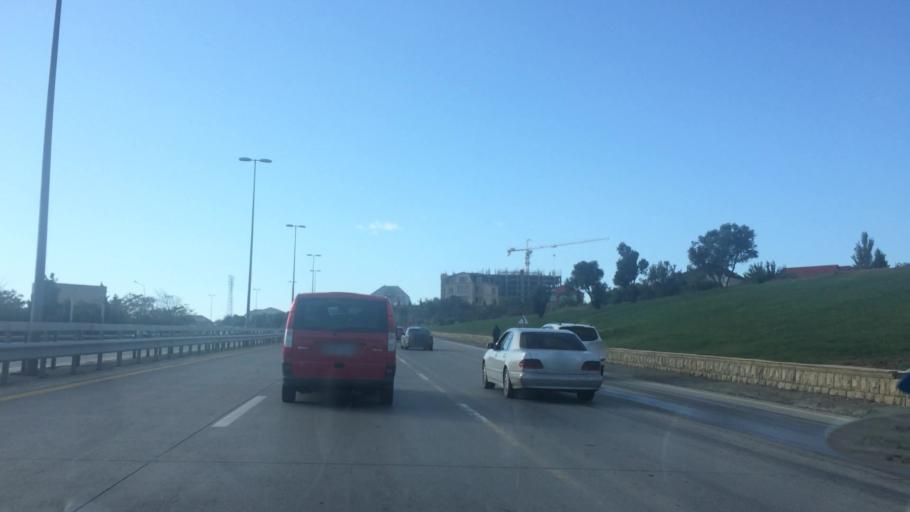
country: AZ
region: Baki
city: Qaracuxur
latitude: 40.3480
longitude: 49.9670
